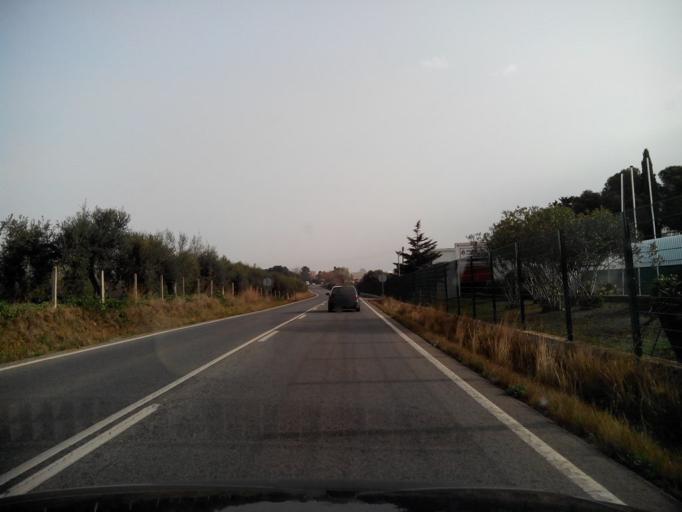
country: ES
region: Catalonia
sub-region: Provincia de Tarragona
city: Riudoms
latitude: 41.1100
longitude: 1.0891
